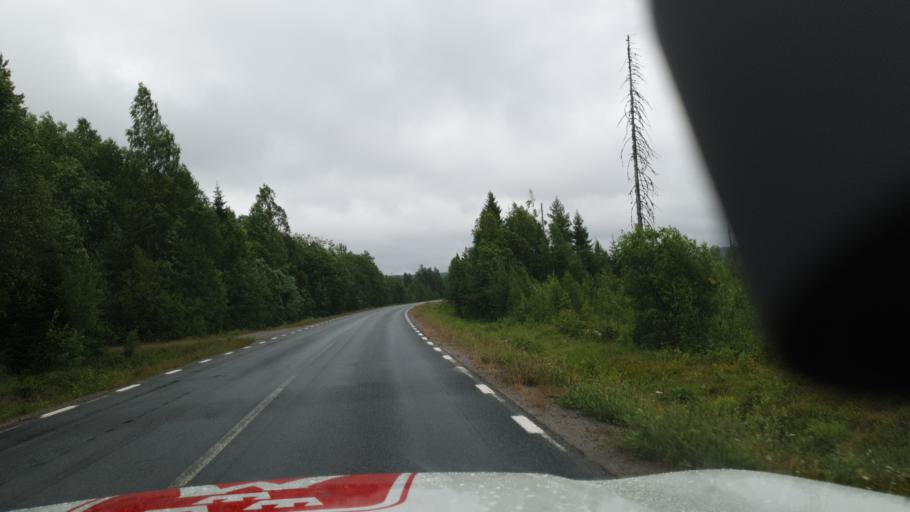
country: SE
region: Vaesterbotten
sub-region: Vannas Kommun
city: Vaennaes
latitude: 63.7753
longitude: 19.7254
